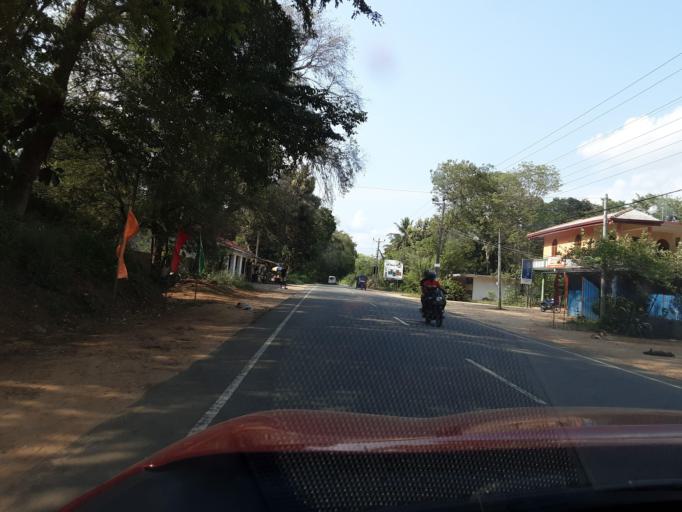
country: LK
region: Uva
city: Haputale
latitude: 6.5856
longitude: 81.1410
